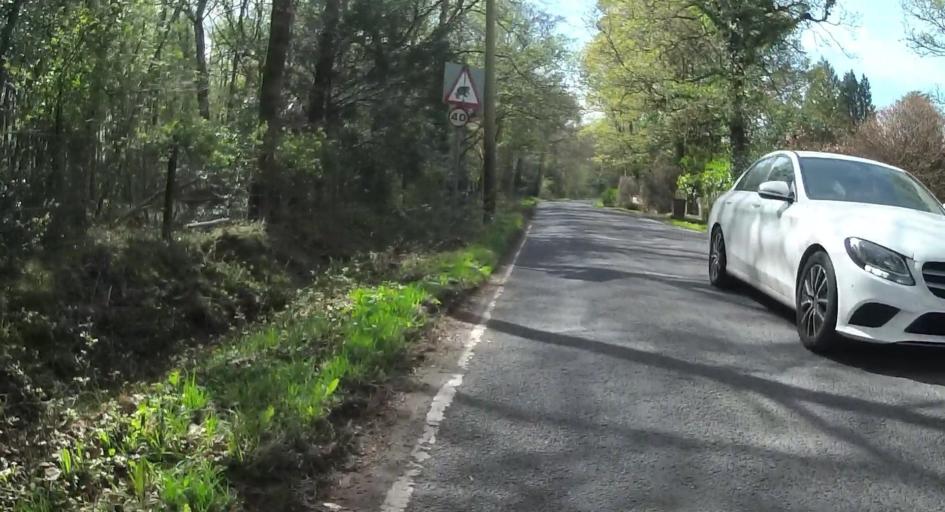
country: GB
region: England
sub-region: Surrey
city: Farnham
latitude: 51.1796
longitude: -0.8063
